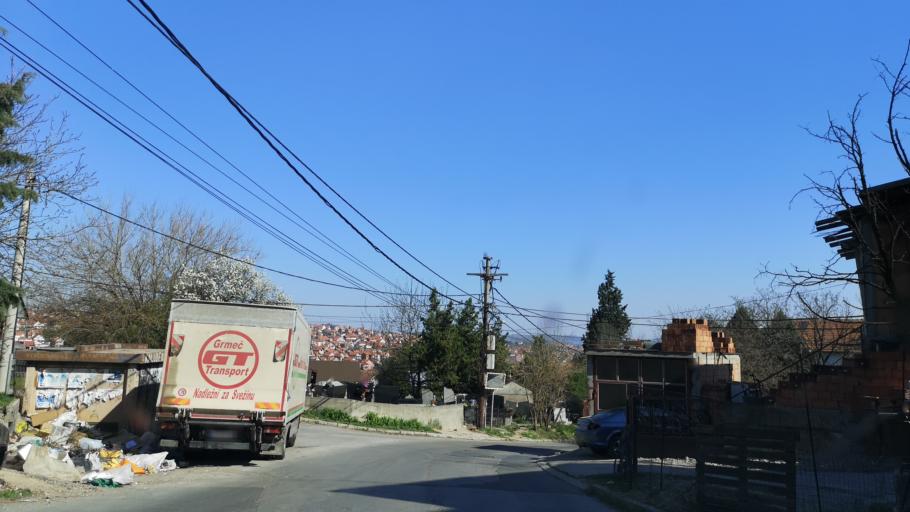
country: RS
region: Central Serbia
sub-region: Belgrade
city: Zvezdara
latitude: 44.7609
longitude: 20.5450
